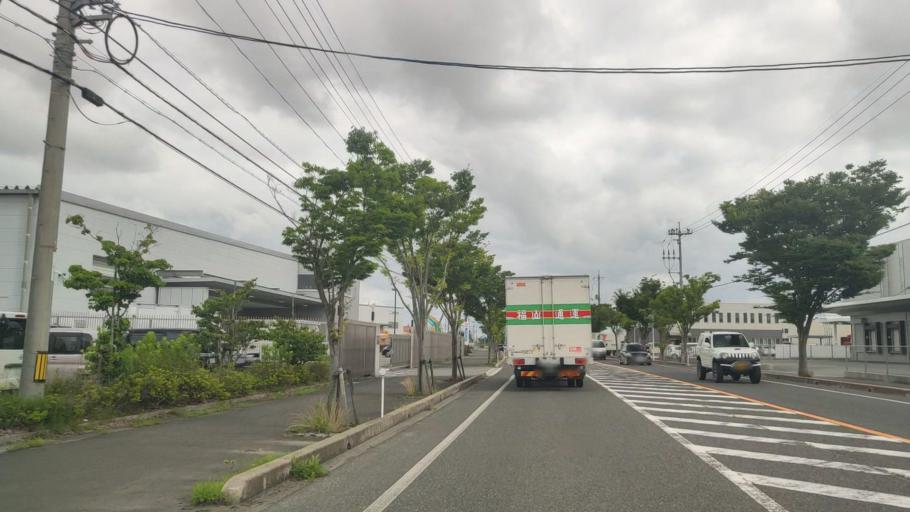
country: JP
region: Tottori
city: Yonago
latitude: 35.4299
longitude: 133.3939
